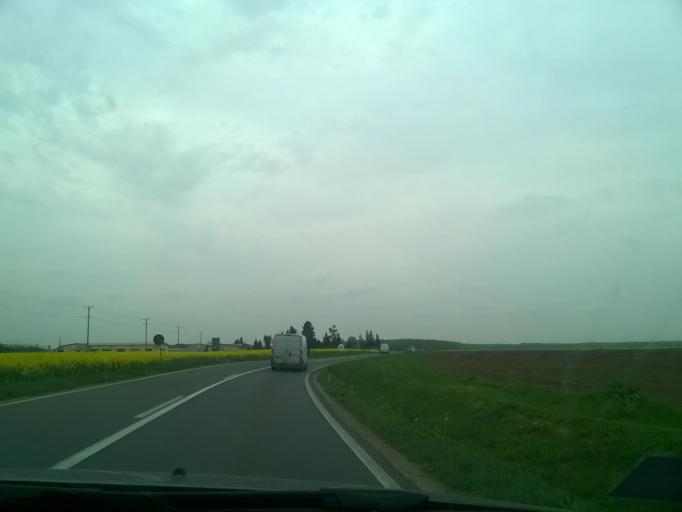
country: RS
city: Hrtkovci
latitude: 44.8516
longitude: 19.7709
